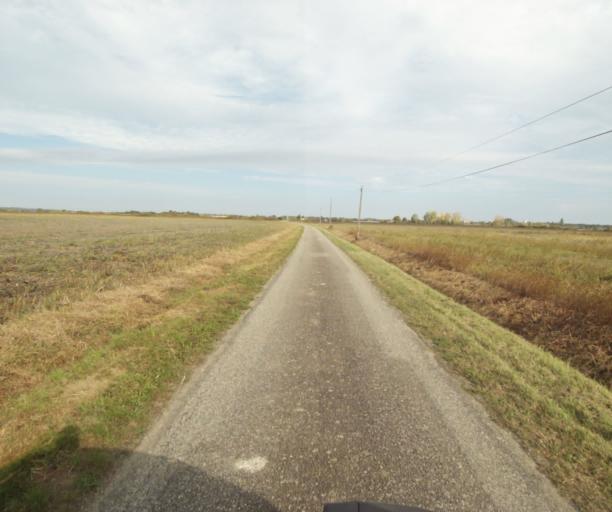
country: FR
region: Midi-Pyrenees
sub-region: Departement du Tarn-et-Garonne
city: Finhan
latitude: 43.9332
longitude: 1.2248
